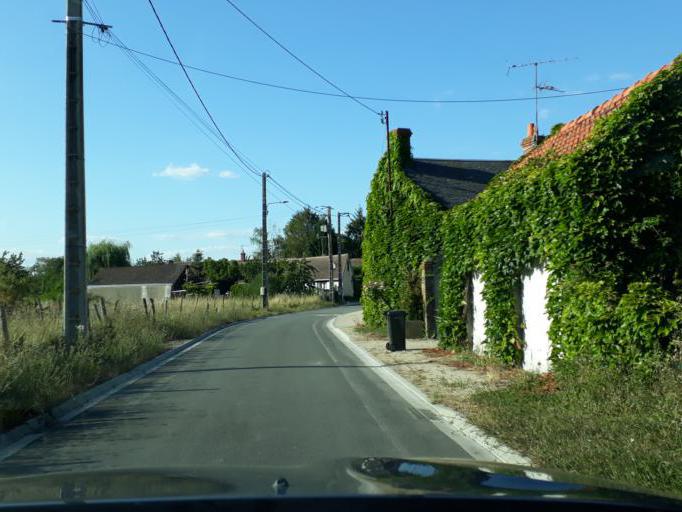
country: FR
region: Centre
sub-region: Departement du Loiret
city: Saint-Ay
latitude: 47.8849
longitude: 1.7358
